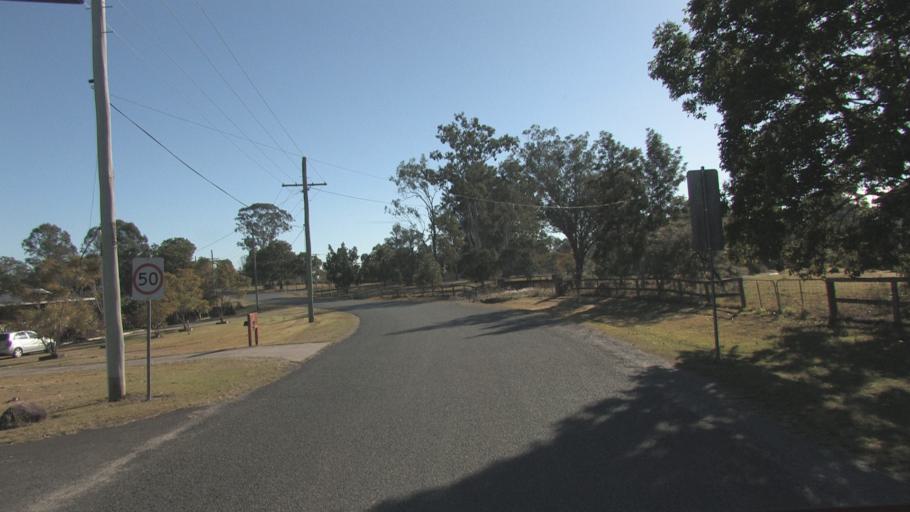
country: AU
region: Queensland
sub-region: Logan
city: Chambers Flat
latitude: -27.7627
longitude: 153.1051
